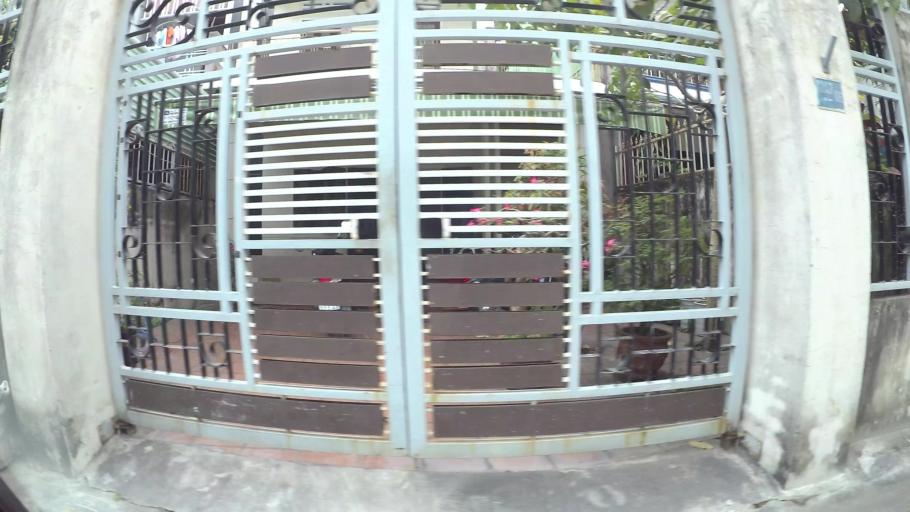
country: VN
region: Da Nang
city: Da Nang
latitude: 16.0533
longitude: 108.2102
